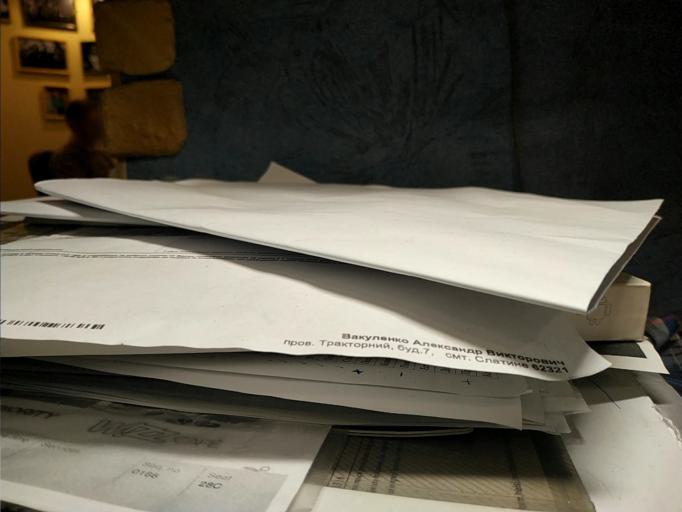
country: RU
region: Tverskaya
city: Zubtsov
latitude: 56.1335
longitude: 34.4969
